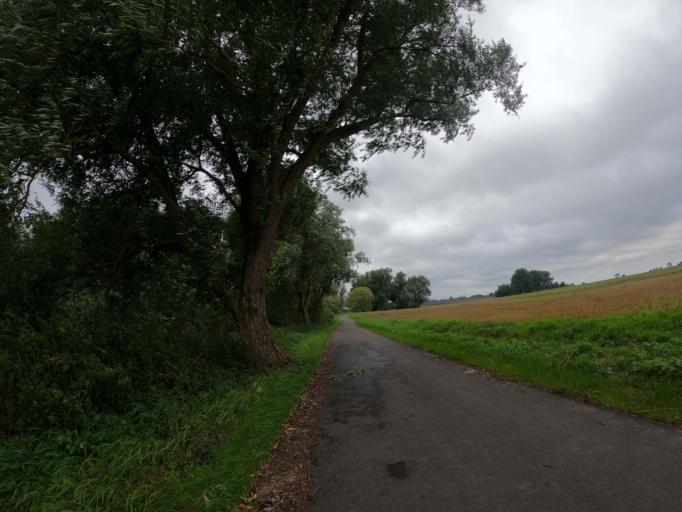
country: DE
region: Mecklenburg-Vorpommern
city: Rambin
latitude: 54.3138
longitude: 13.1879
